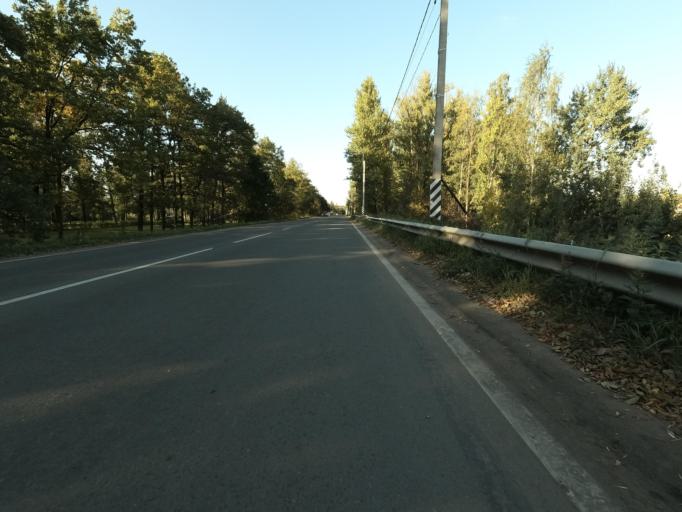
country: RU
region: St.-Petersburg
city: Kolpino
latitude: 59.7502
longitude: 30.6159
